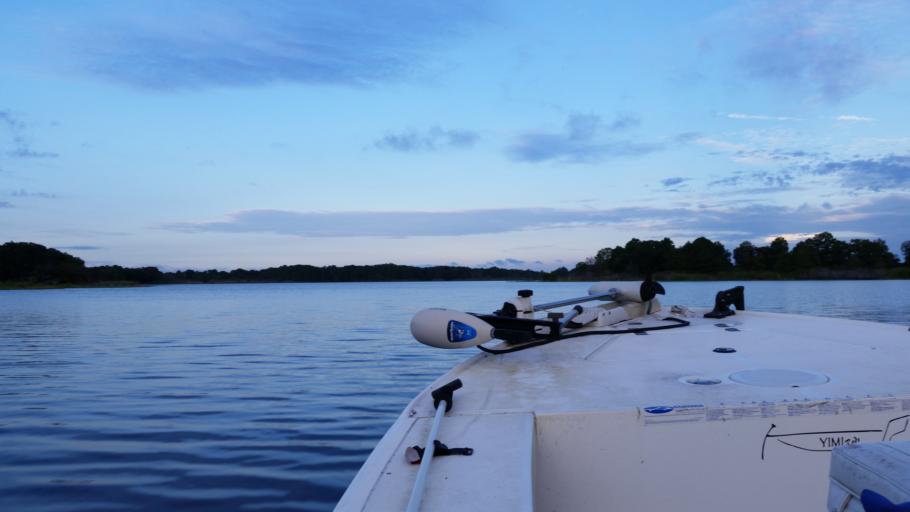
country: US
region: Florida
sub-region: Citrus County
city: Inverness
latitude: 28.8313
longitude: -82.3073
